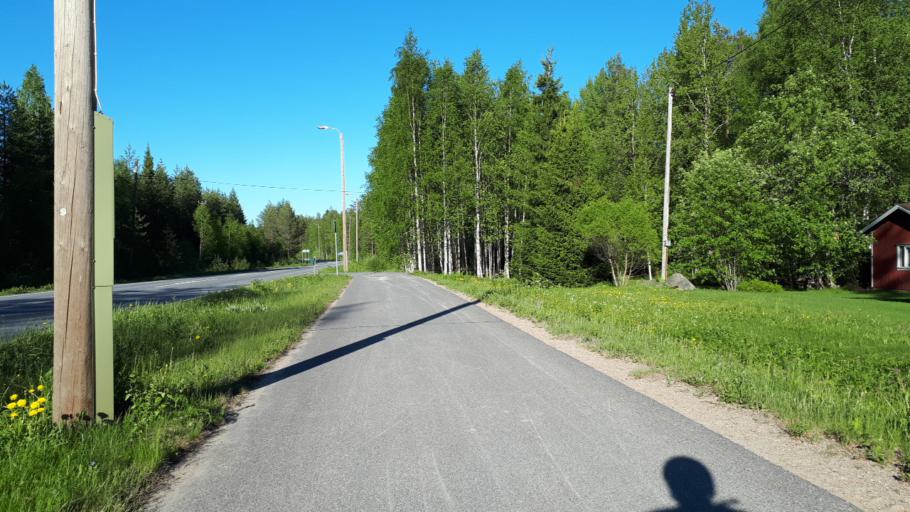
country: FI
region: Northern Ostrobothnia
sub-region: Oulunkaari
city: Ii
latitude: 65.3254
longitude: 25.5131
